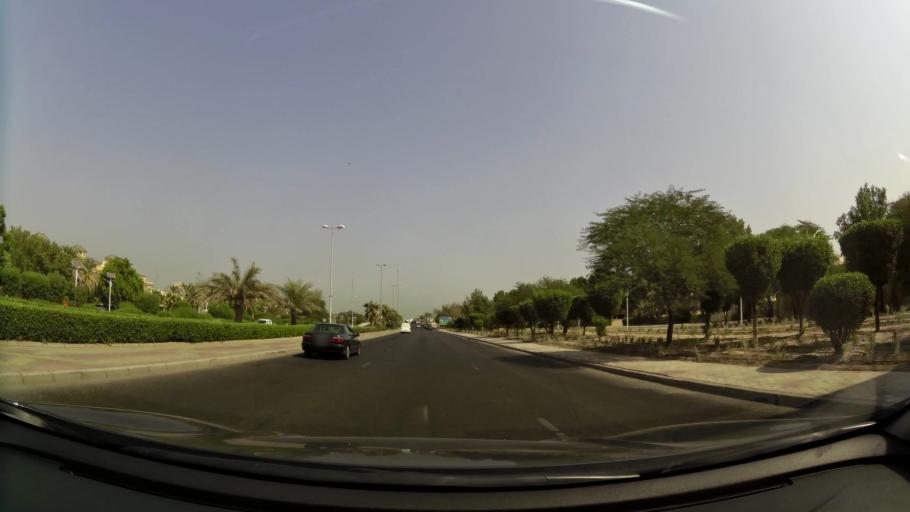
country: KW
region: Al Asimah
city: Ad Dasmah
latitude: 29.3483
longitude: 47.9902
